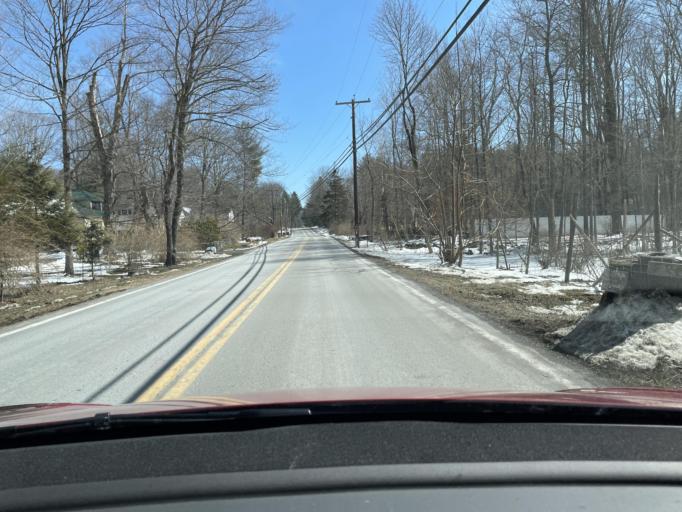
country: US
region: New York
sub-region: Ulster County
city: Woodstock
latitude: 42.0688
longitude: -74.1922
